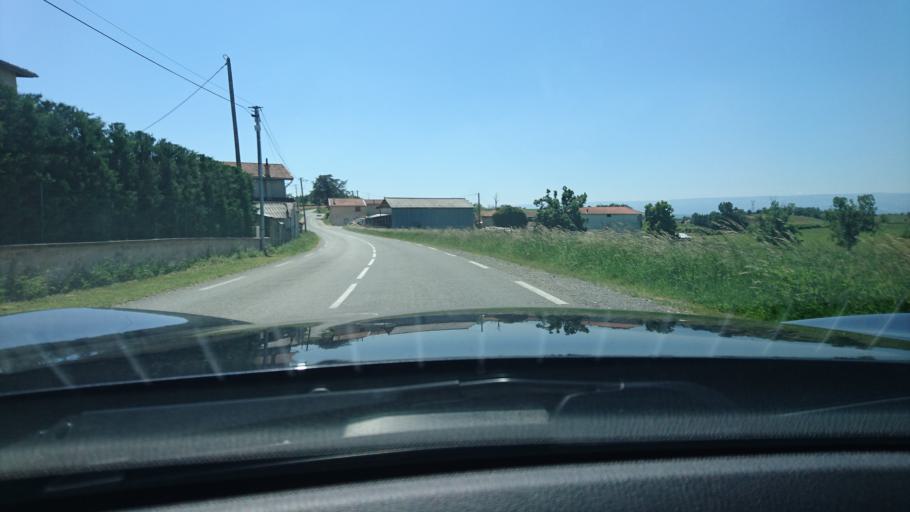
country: FR
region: Rhone-Alpes
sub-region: Departement de la Loire
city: Rozier-en-Donzy
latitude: 45.7843
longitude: 4.2814
